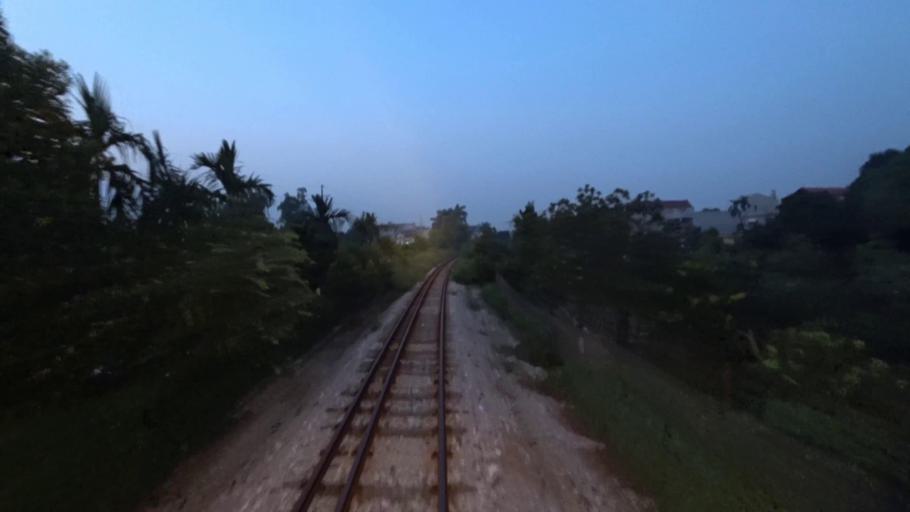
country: VN
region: Ha Noi
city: Soc Son
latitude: 21.2503
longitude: 105.8617
